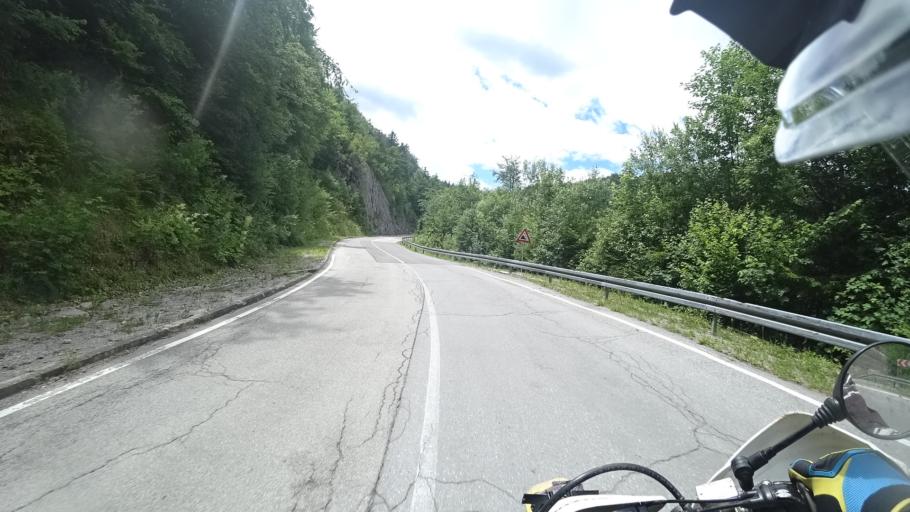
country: SI
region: Osilnica
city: Osilnica
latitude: 45.5998
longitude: 14.6358
